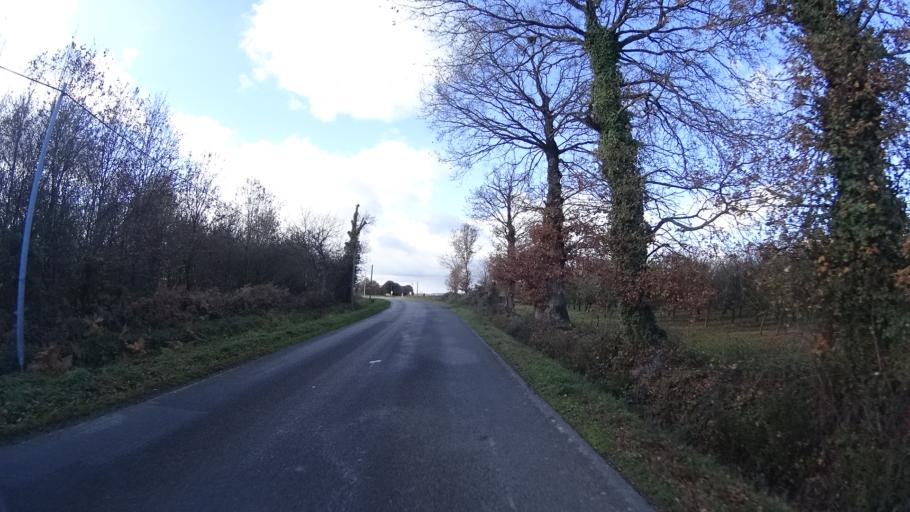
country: FR
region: Brittany
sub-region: Departement du Morbihan
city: Carentoir
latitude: 47.8382
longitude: -2.1160
